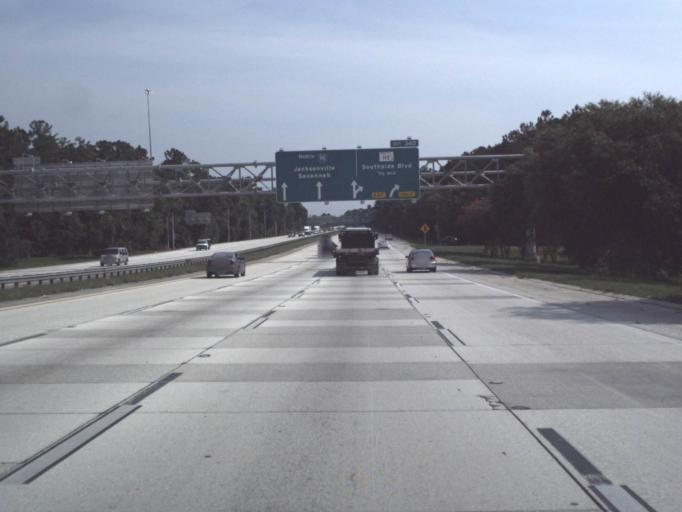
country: US
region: Florida
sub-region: Saint Johns County
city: Fruit Cove
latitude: 30.1860
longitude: -81.5577
